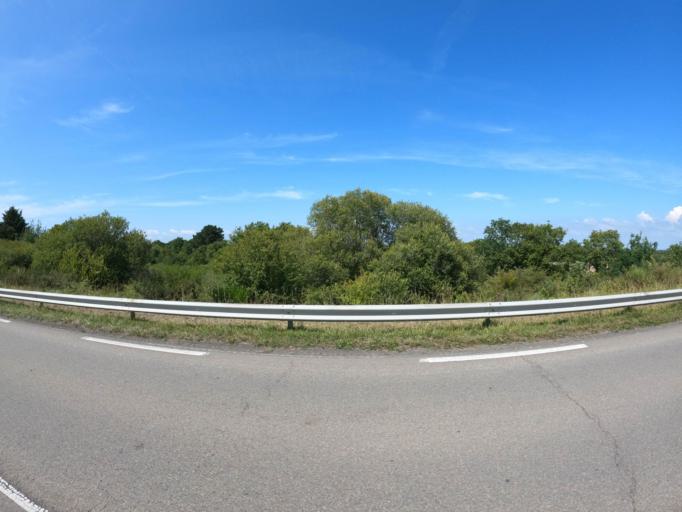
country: FR
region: Pays de la Loire
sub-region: Departement de la Loire-Atlantique
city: La Bernerie-en-Retz
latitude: 47.1042
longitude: -2.0474
